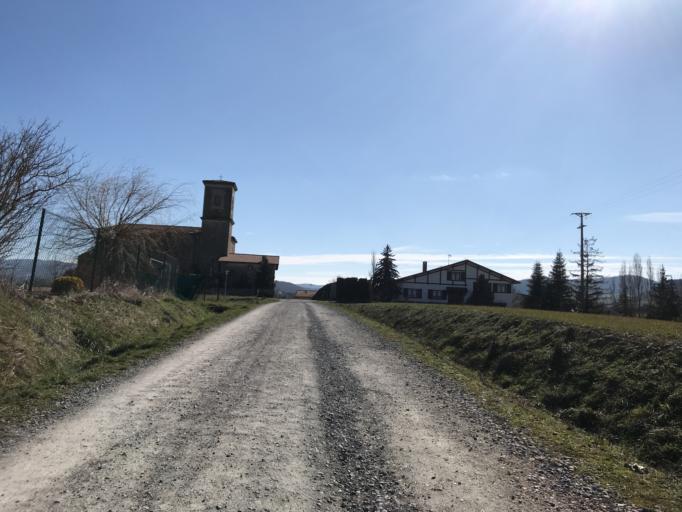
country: ES
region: Basque Country
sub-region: Provincia de Alava
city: Gasteiz / Vitoria
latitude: 42.8206
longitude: -2.6531
